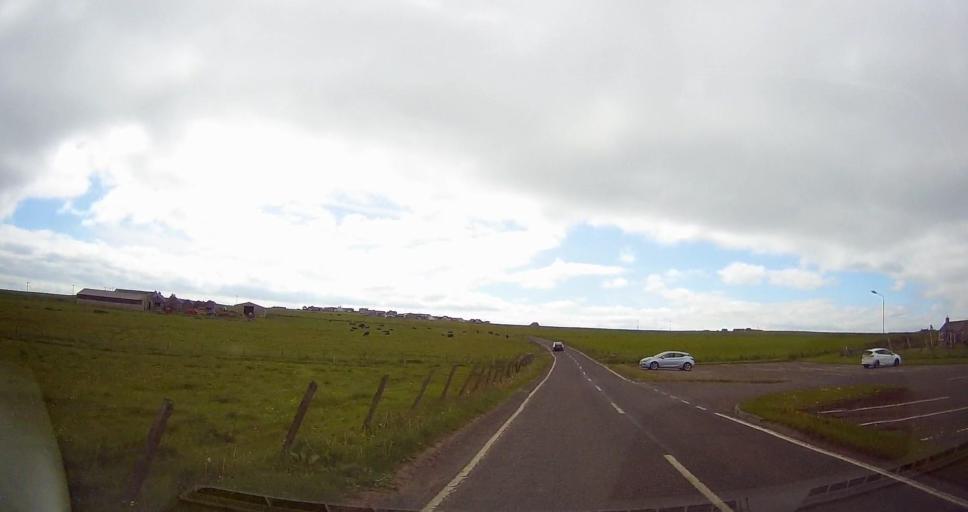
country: GB
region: Scotland
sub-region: Orkney Islands
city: Kirkwall
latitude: 58.9363
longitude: -2.7470
